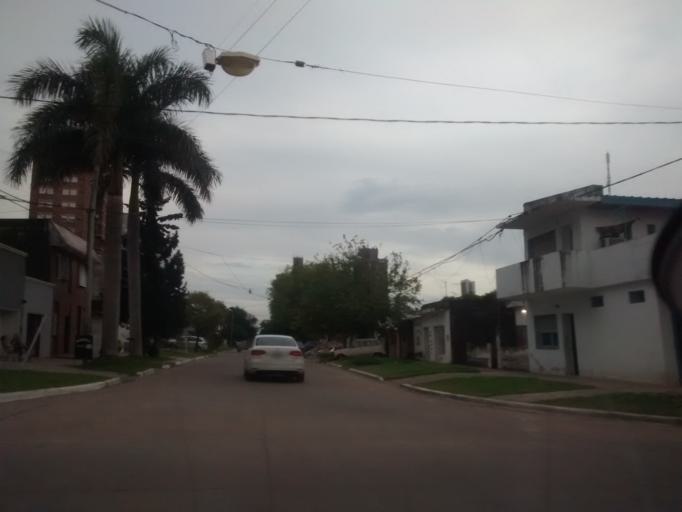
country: AR
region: Chaco
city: Resistencia
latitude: -27.4575
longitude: -58.9971
